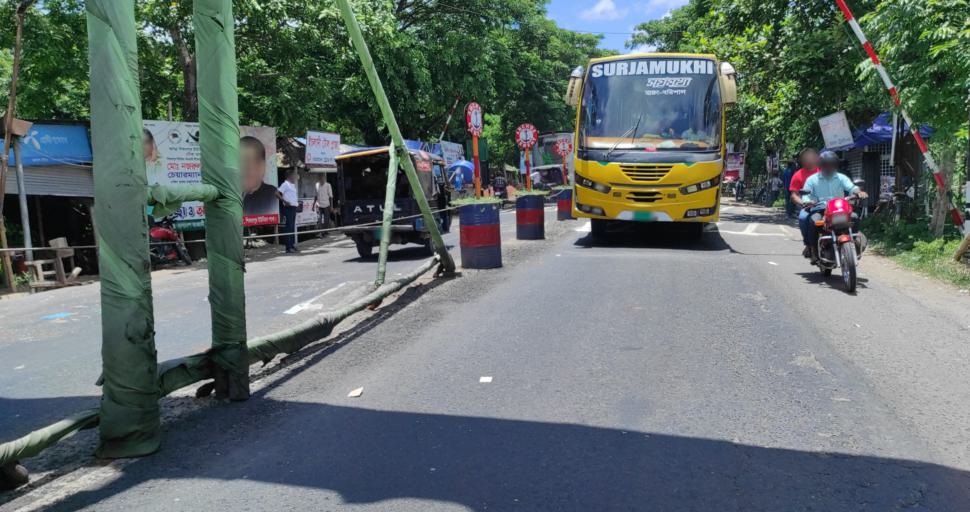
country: BD
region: Barisal
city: Gaurnadi
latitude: 22.8308
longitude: 90.2571
